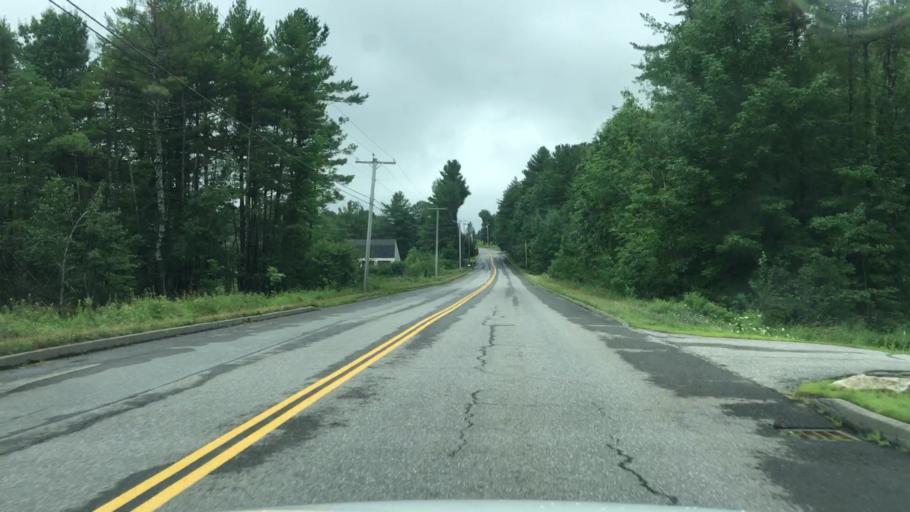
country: US
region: Maine
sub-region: Kennebec County
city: Augusta
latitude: 44.3125
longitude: -69.7395
